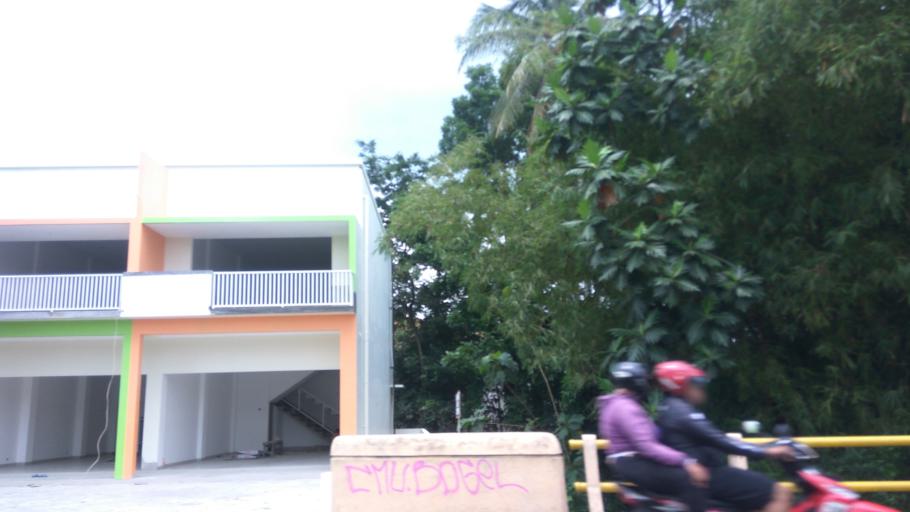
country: ID
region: Daerah Istimewa Yogyakarta
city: Melati
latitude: -7.7202
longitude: 110.4036
